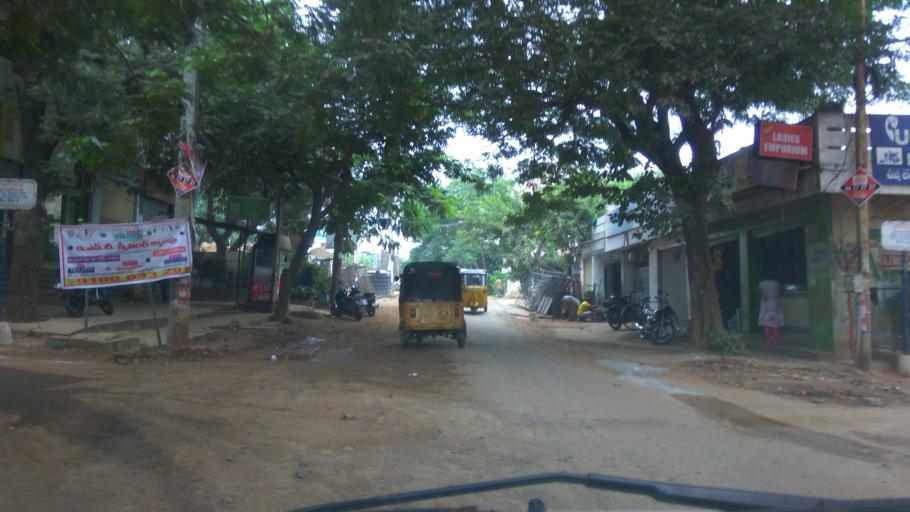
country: IN
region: Telangana
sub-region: Hyderabad
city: Malkajgiri
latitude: 17.4536
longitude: 78.5292
